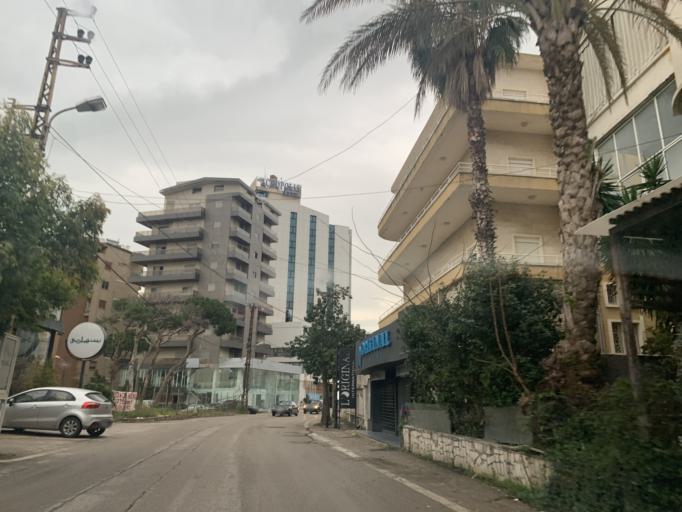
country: LB
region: Mont-Liban
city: Djounie
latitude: 33.9821
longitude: 35.6169
